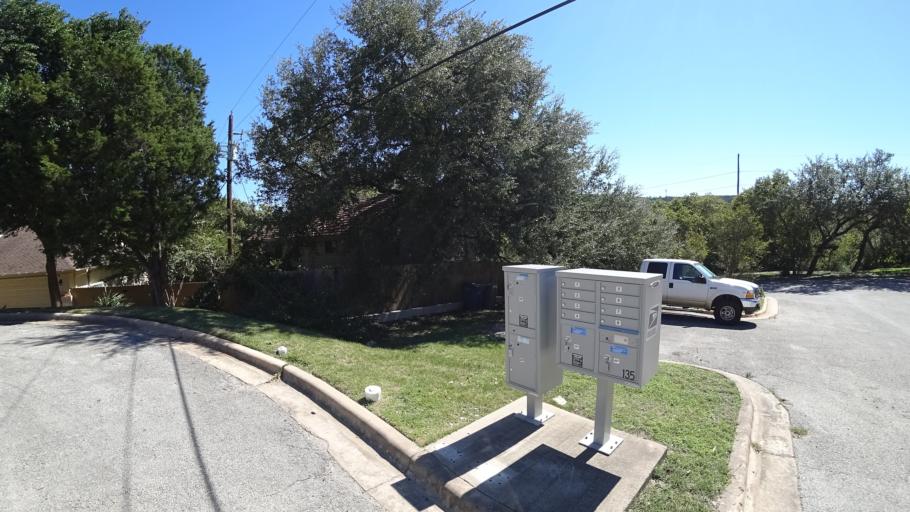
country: US
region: Texas
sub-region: Travis County
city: West Lake Hills
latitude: 30.3406
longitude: -97.7740
